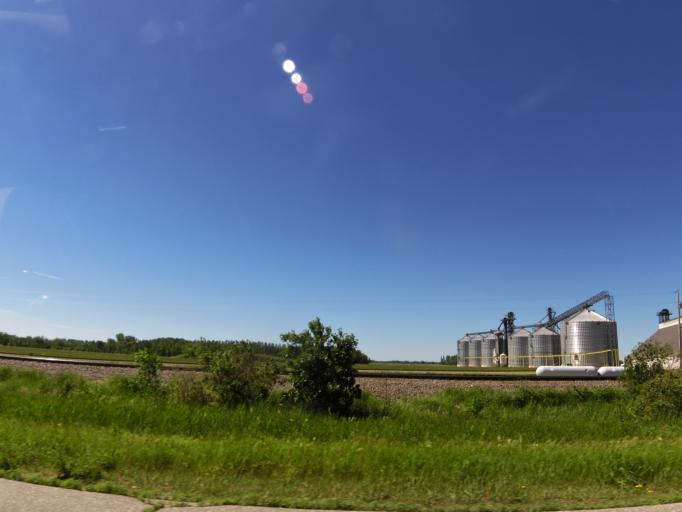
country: US
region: Minnesota
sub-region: Red Lake County
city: Red Lake Falls
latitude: 47.6880
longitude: -96.0693
